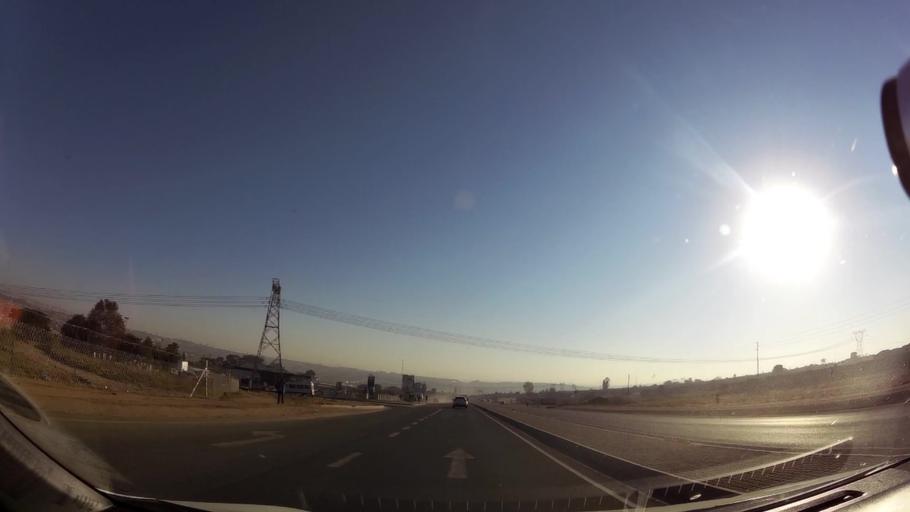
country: ZA
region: Gauteng
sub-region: City of Johannesburg Metropolitan Municipality
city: Midrand
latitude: -25.9271
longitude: 28.0979
